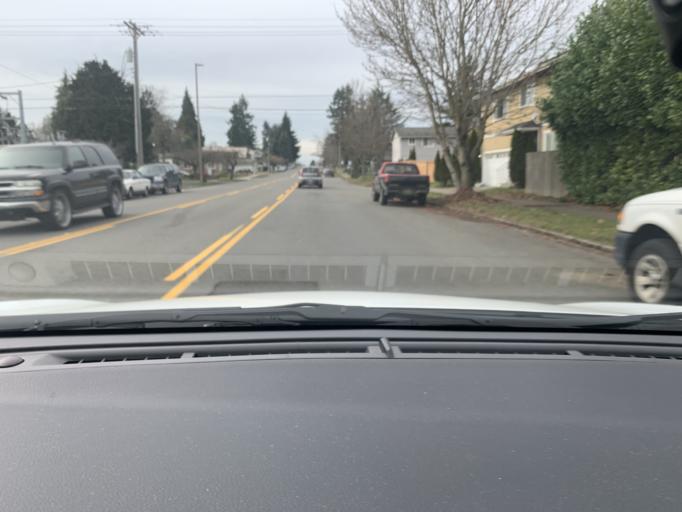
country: US
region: Washington
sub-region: Pierce County
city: Tacoma
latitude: 47.2516
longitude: -122.4562
